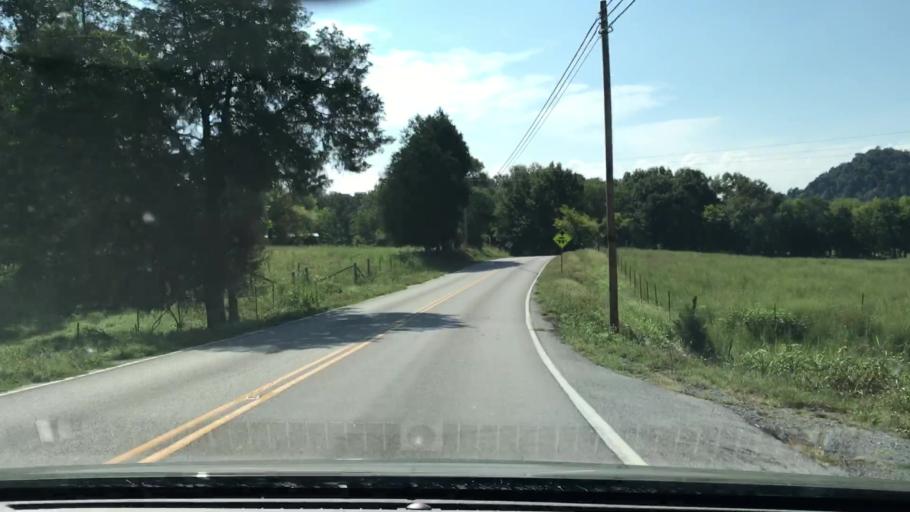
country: US
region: Tennessee
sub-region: Jackson County
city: Gainesboro
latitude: 36.3537
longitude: -85.7131
